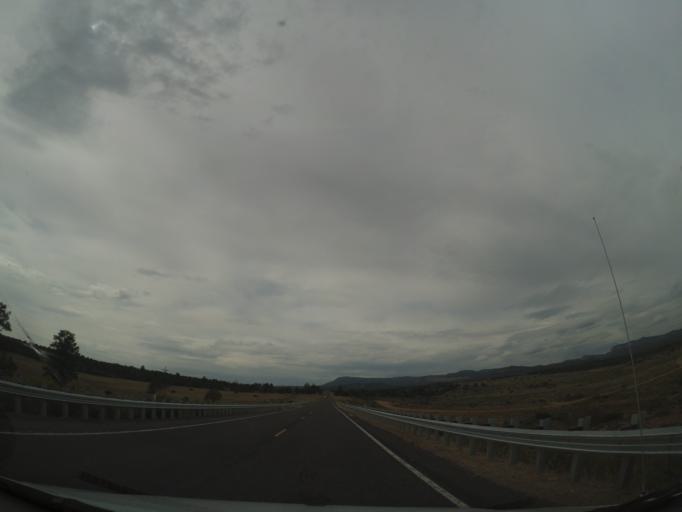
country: US
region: Utah
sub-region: Kane County
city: Kanab
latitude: 37.2321
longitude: -112.7342
